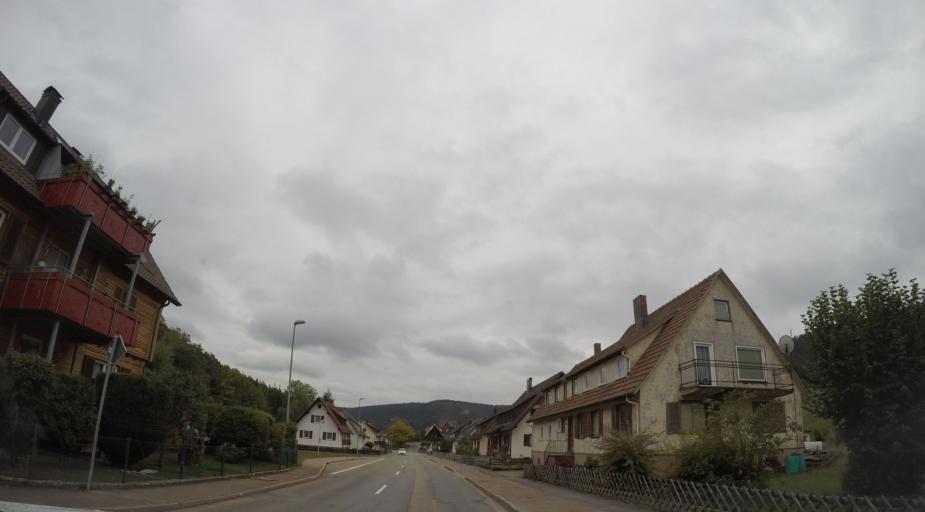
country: DE
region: Baden-Wuerttemberg
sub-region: Karlsruhe Region
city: Baiersbronn
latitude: 48.5250
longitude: 8.3637
